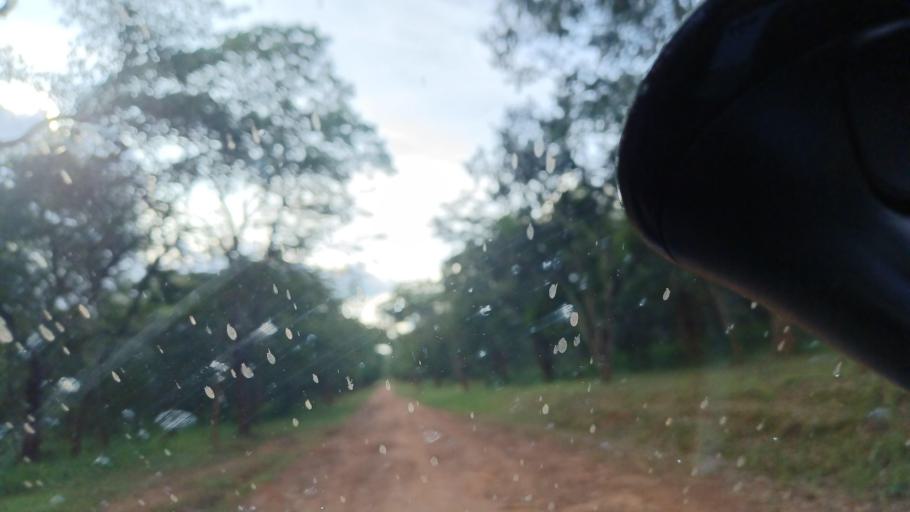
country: ZM
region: North-Western
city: Kasempa
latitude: -13.5991
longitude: 26.1390
